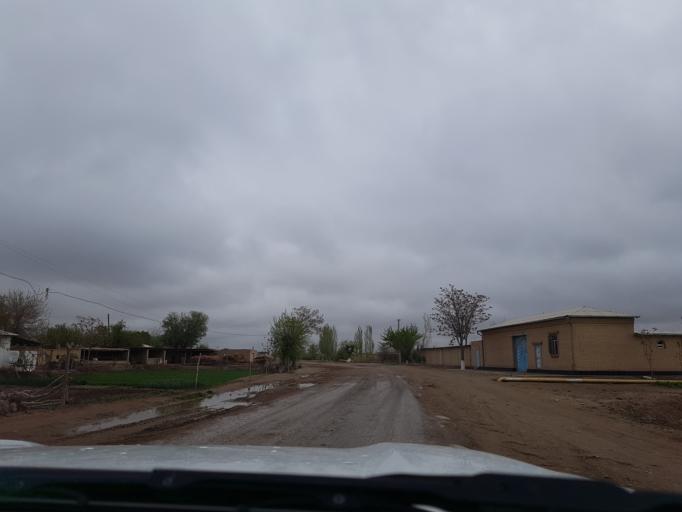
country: TM
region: Lebap
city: Sayat
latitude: 38.4542
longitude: 64.3668
